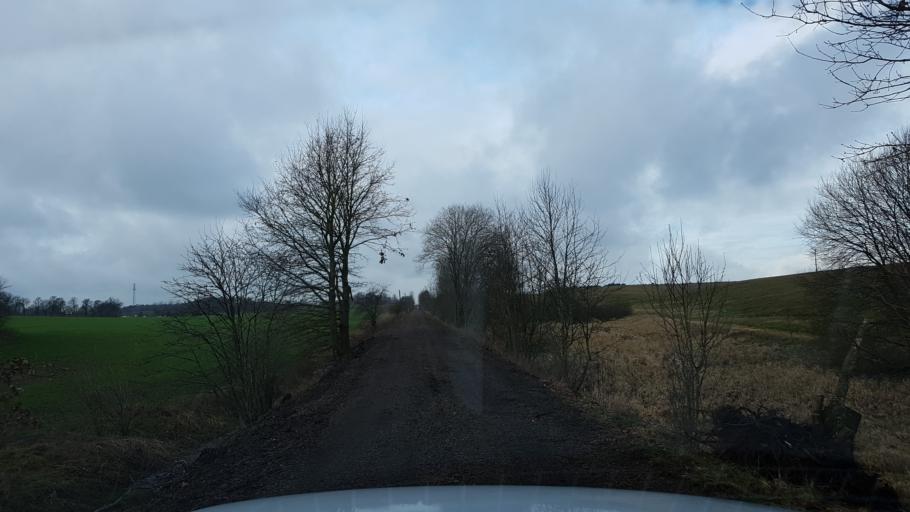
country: PL
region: West Pomeranian Voivodeship
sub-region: Powiat swidwinski
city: Polczyn-Zdroj
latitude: 53.7827
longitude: 16.0636
